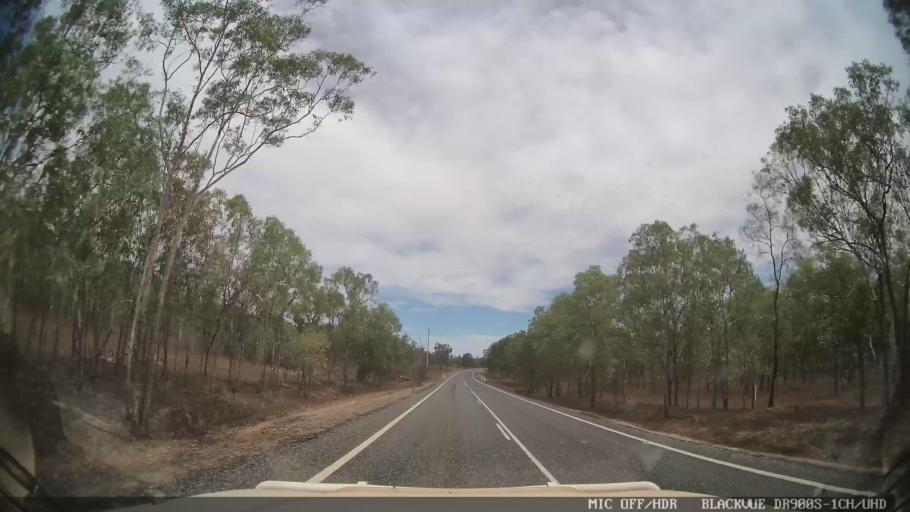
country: AU
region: Queensland
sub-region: Cairns
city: Port Douglas
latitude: -16.2490
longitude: 144.7263
